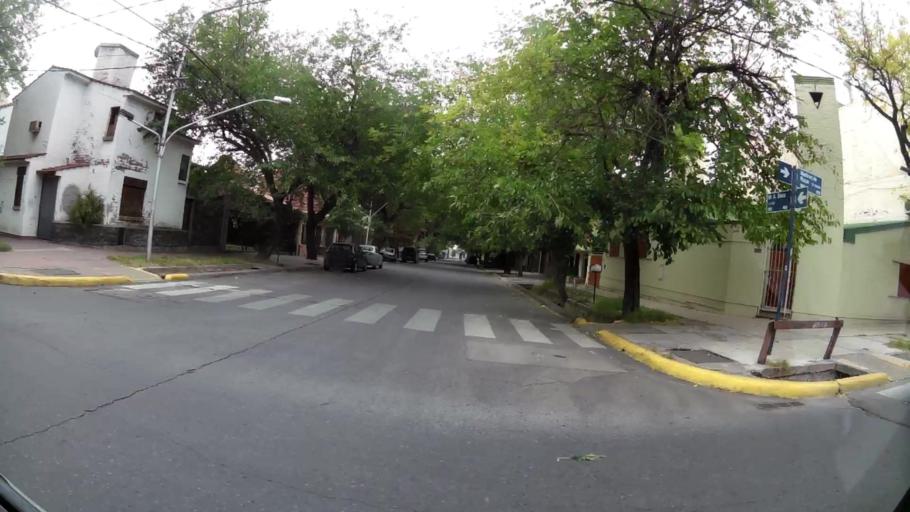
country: AR
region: Mendoza
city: Mendoza
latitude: -32.8942
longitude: -68.8572
